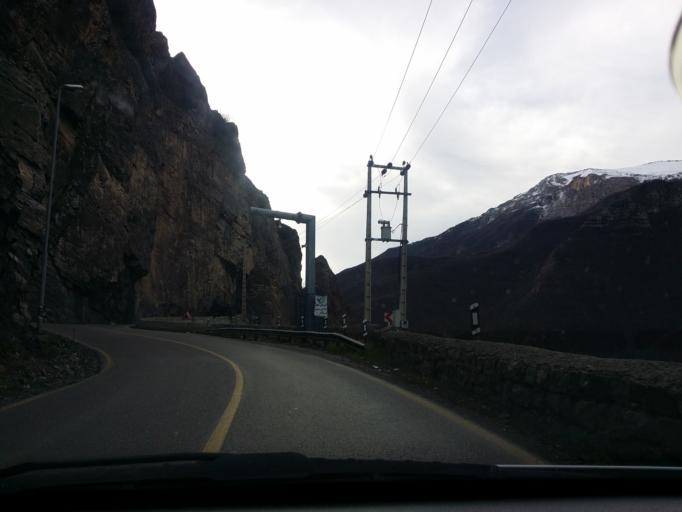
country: IR
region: Mazandaran
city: Chalus
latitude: 36.2556
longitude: 51.2779
